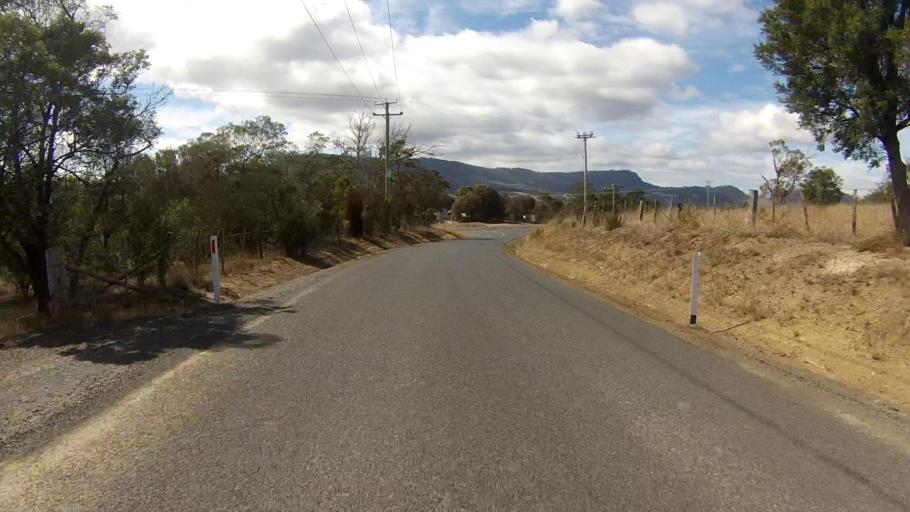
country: AU
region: Tasmania
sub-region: Brighton
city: Old Beach
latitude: -42.7288
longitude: 147.2875
